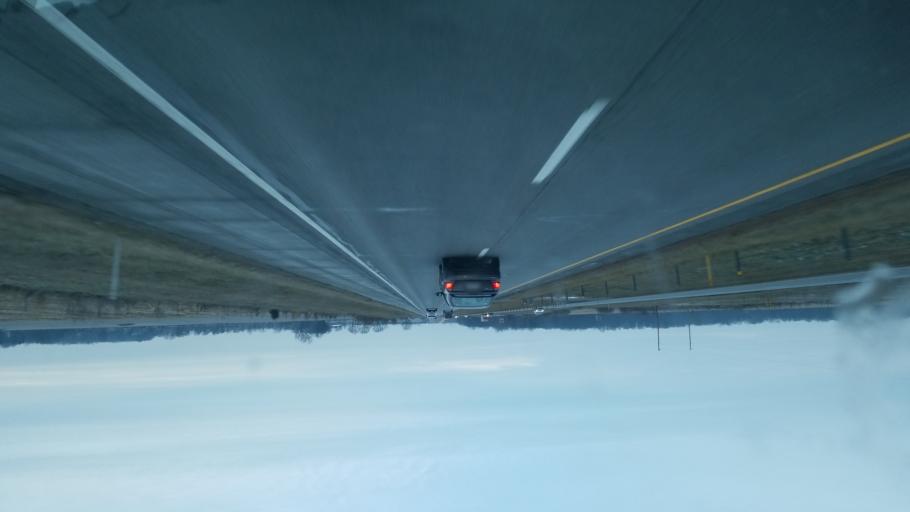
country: US
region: Indiana
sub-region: Henry County
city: Knightstown
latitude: 39.8306
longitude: -85.5859
